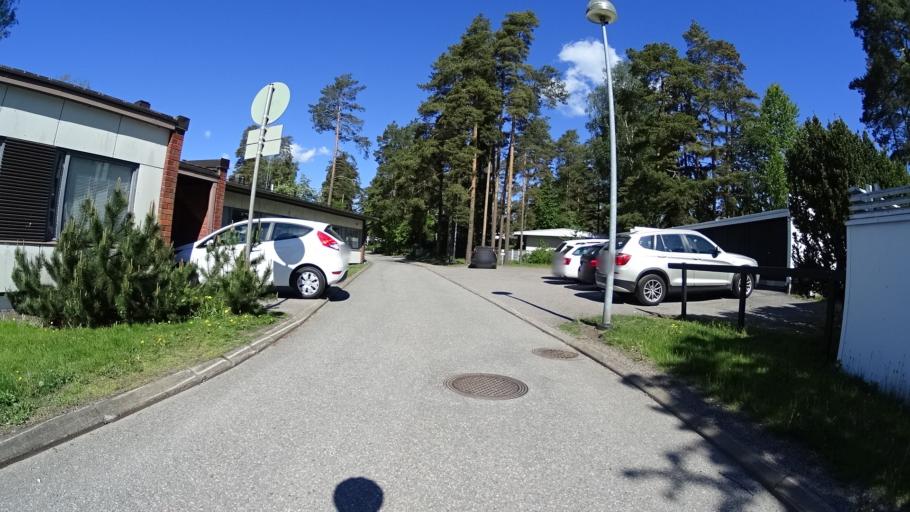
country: FI
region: Uusimaa
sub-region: Helsinki
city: Koukkuniemi
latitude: 60.1643
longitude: 24.7820
